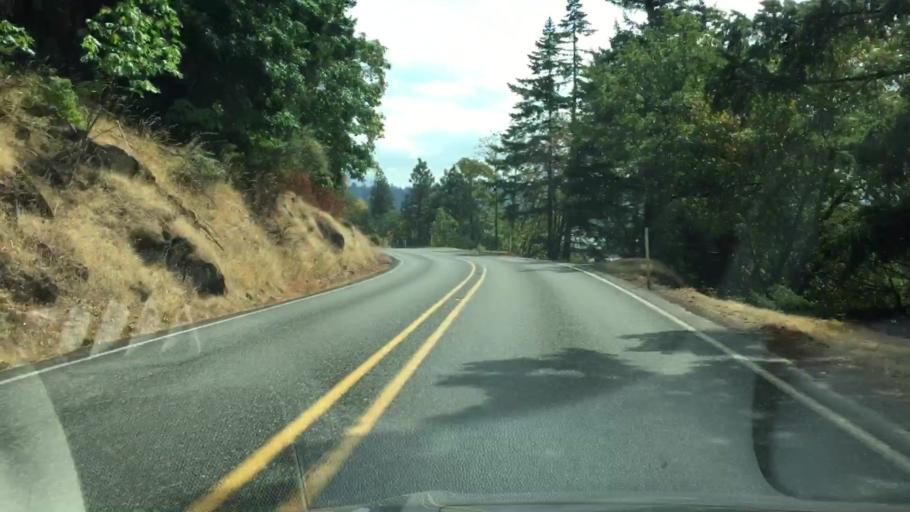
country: US
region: Oregon
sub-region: Hood River County
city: Hood River
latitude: 45.7311
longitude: -121.5203
